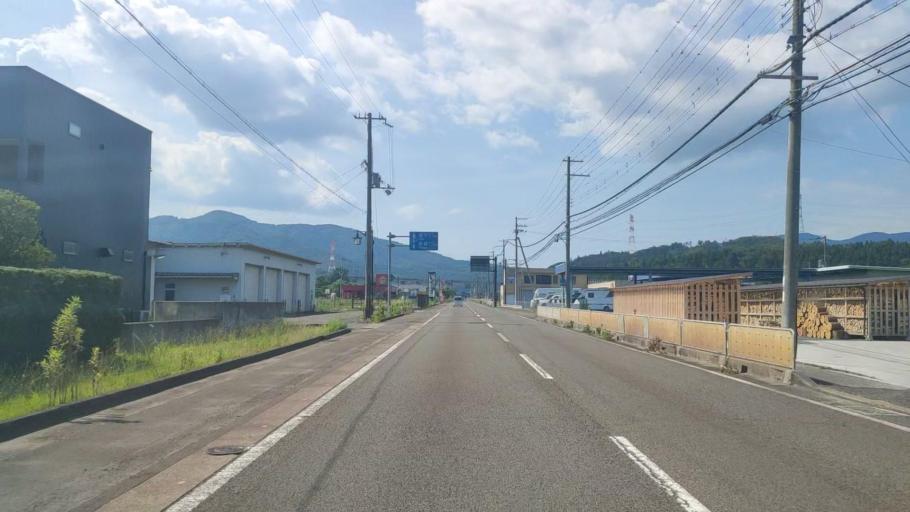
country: JP
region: Fukui
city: Tsuruga
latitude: 35.5246
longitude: 136.1607
